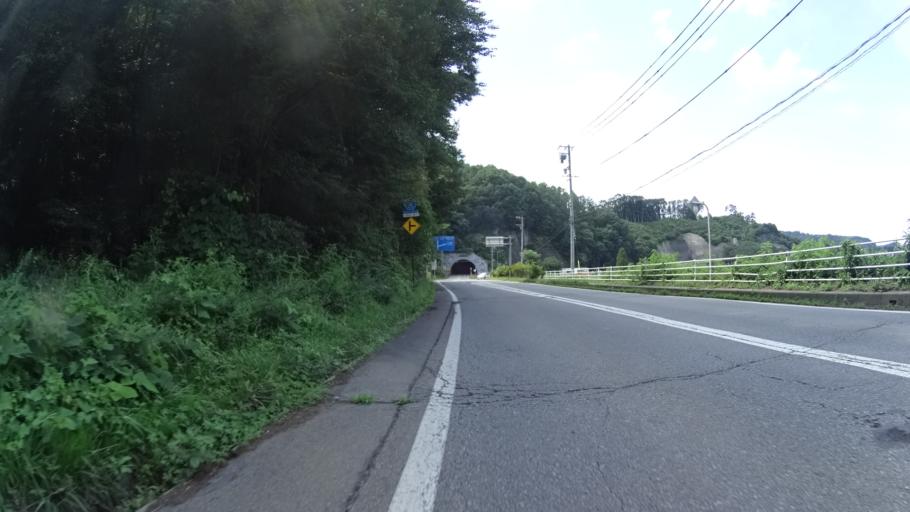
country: JP
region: Nagano
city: Saku
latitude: 36.0819
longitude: 138.4874
